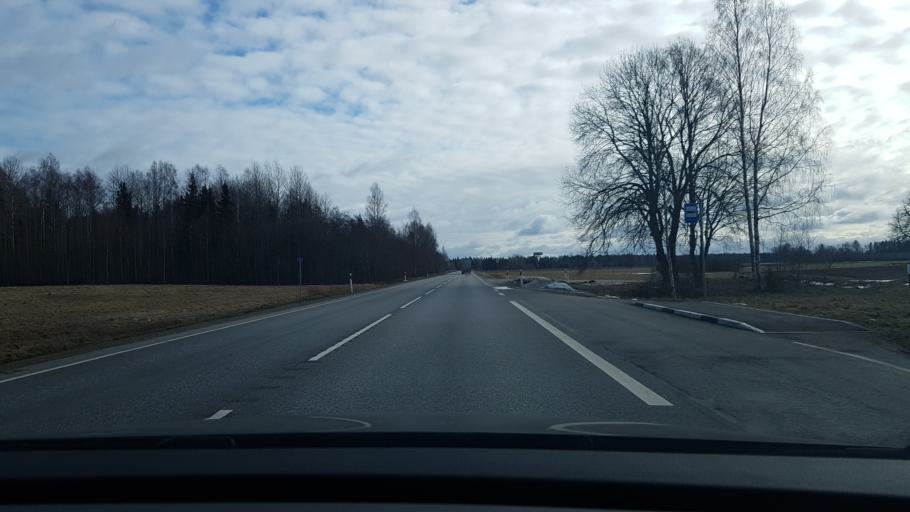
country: EE
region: Viljandimaa
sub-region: Moisakuela linn
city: Moisakula
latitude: 58.1328
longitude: 25.1157
